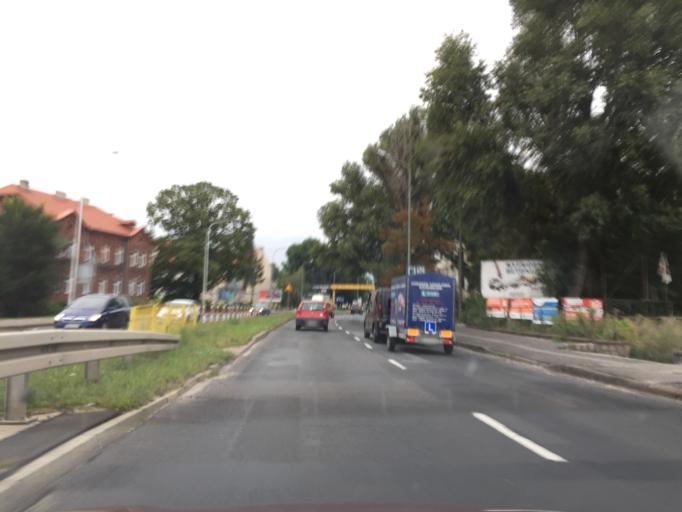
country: PL
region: Greater Poland Voivodeship
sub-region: Kalisz
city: Kalisz
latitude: 51.7632
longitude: 18.0787
